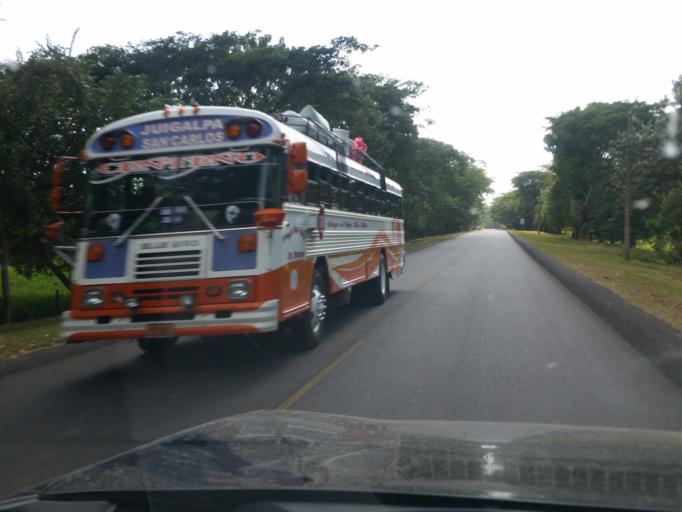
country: NI
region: Rio San Juan
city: San Miguelito
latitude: 11.5192
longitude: -84.8325
